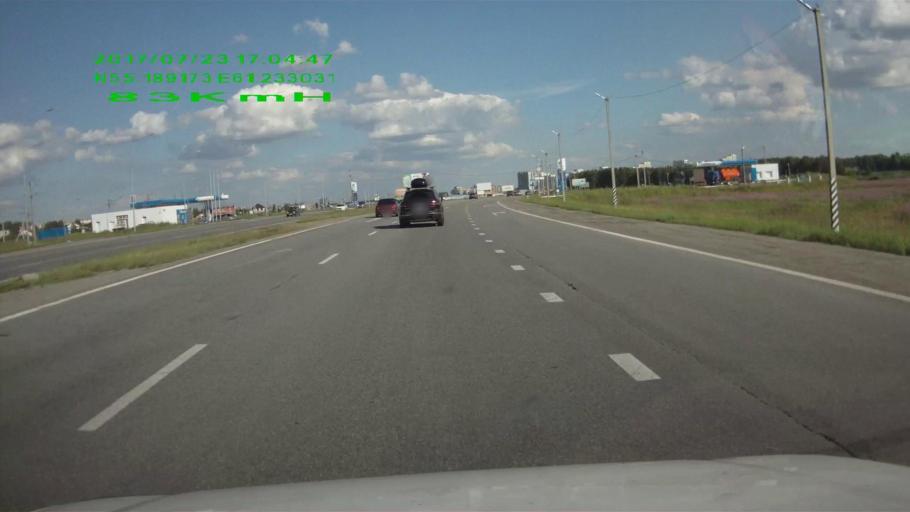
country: RU
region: Chelyabinsk
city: Roshchino
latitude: 55.1887
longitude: 61.2345
